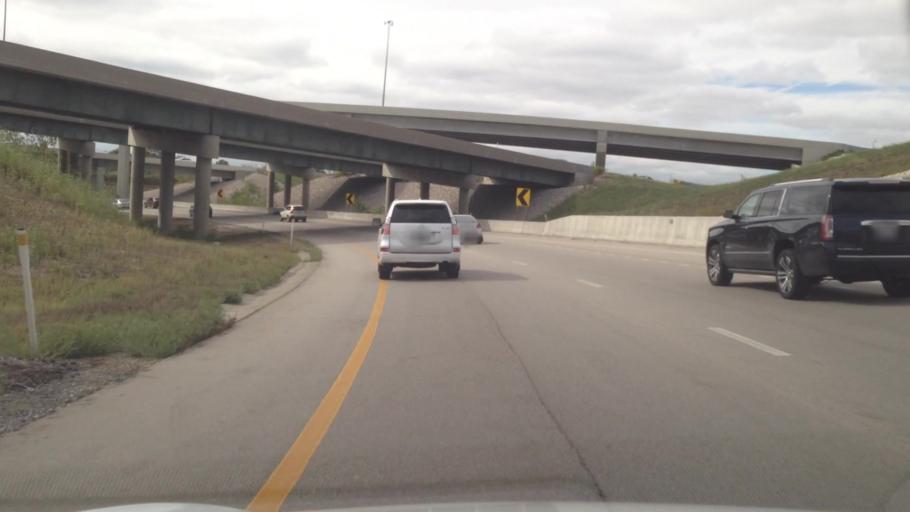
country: US
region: Kansas
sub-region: Johnson County
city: Lenexa
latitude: 38.9449
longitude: -94.7703
